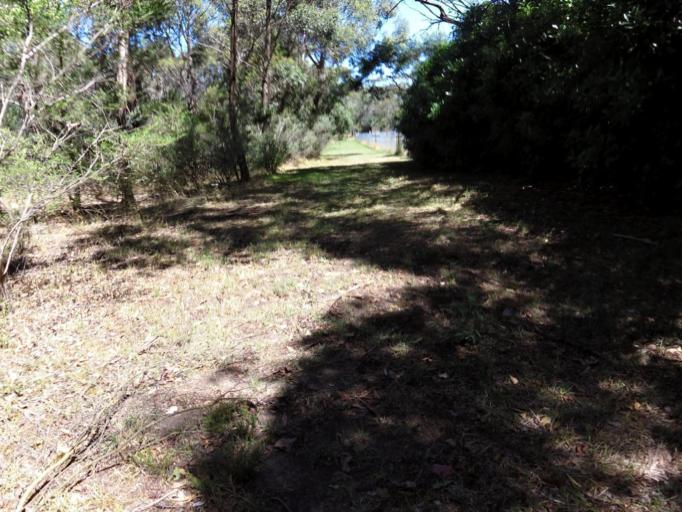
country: AU
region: Victoria
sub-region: Hume
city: Sunbury
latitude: -37.3574
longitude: 144.5489
